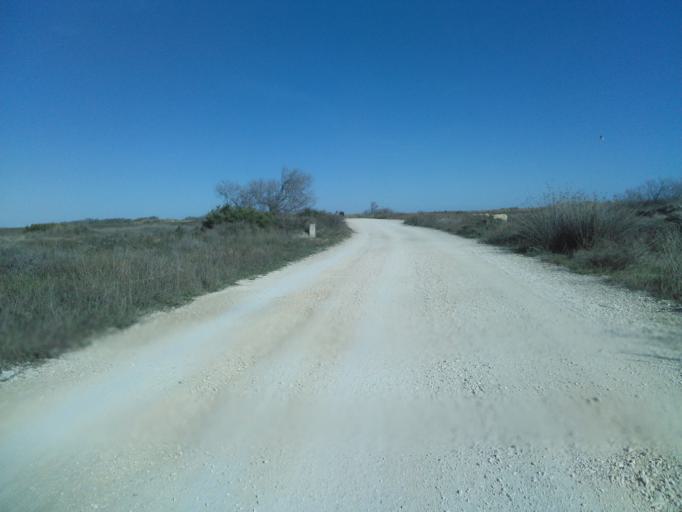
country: FR
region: Provence-Alpes-Cote d'Azur
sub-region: Departement des Bouches-du-Rhone
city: Saintes-Maries-de-la-Mer
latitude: 43.4597
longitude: 4.4910
